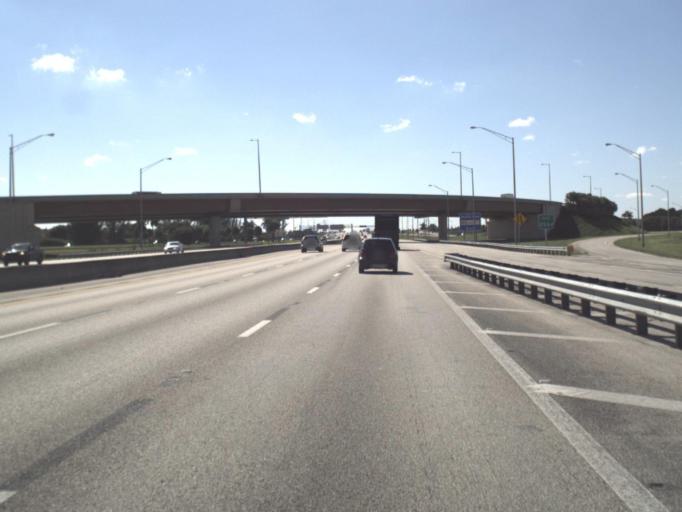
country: US
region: Florida
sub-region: Miami-Dade County
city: Sweetwater
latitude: 25.7784
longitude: -80.3861
